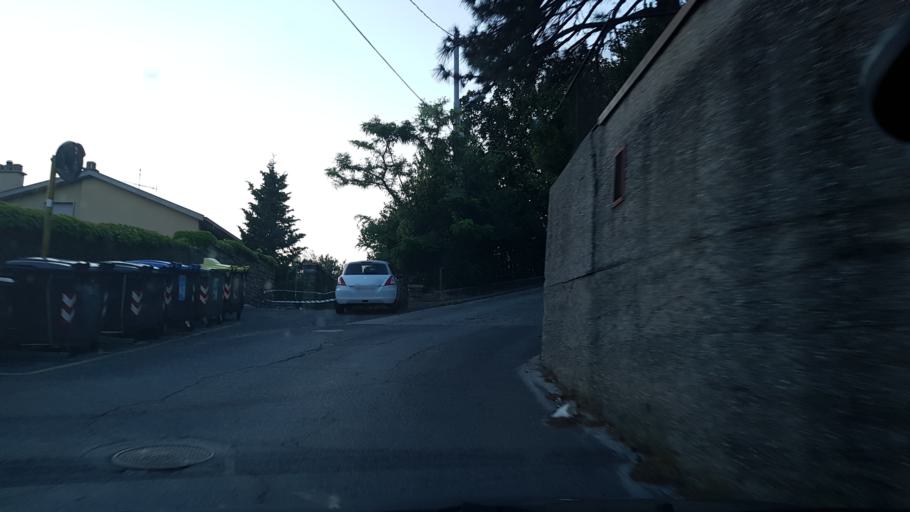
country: IT
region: Friuli Venezia Giulia
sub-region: Provincia di Trieste
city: Villa Opicina
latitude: 45.6727
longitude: 13.7621
